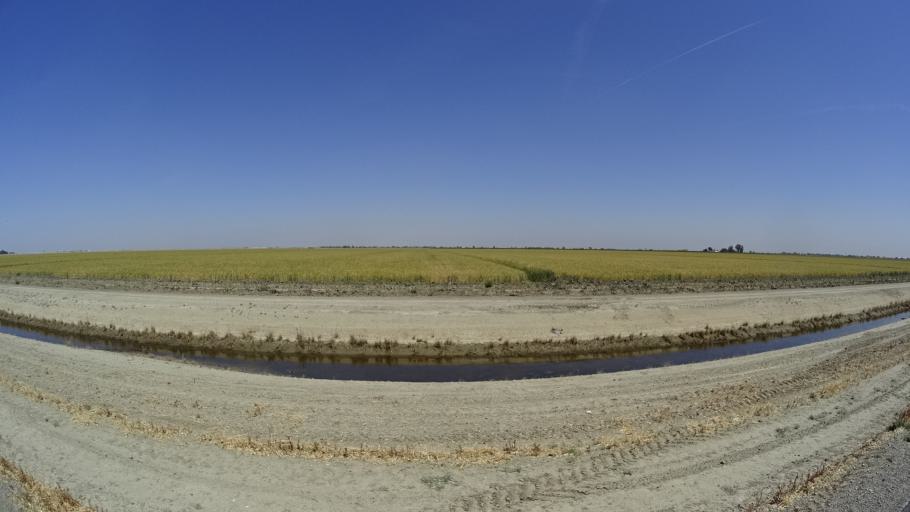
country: US
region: California
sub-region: Kings County
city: Corcoran
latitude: 36.0217
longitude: -119.5496
